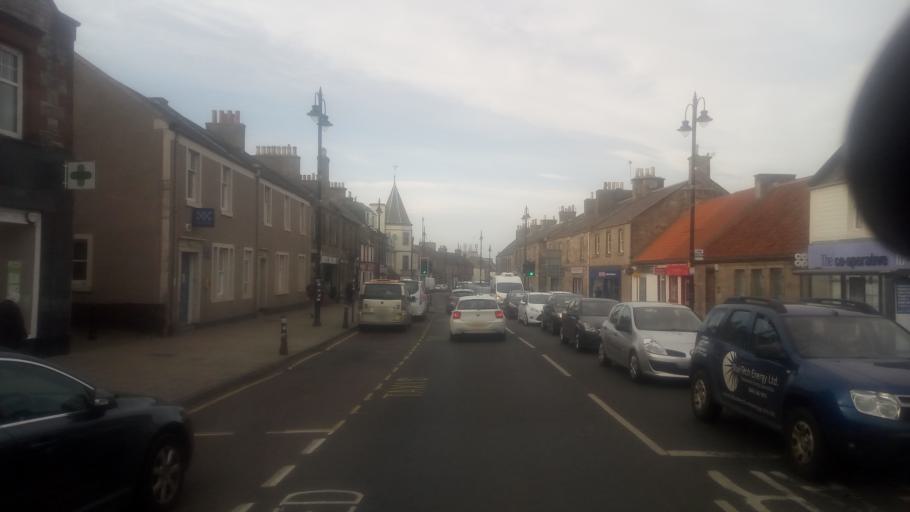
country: GB
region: Scotland
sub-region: East Lothian
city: Tranent
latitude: 55.9433
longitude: -2.9496
